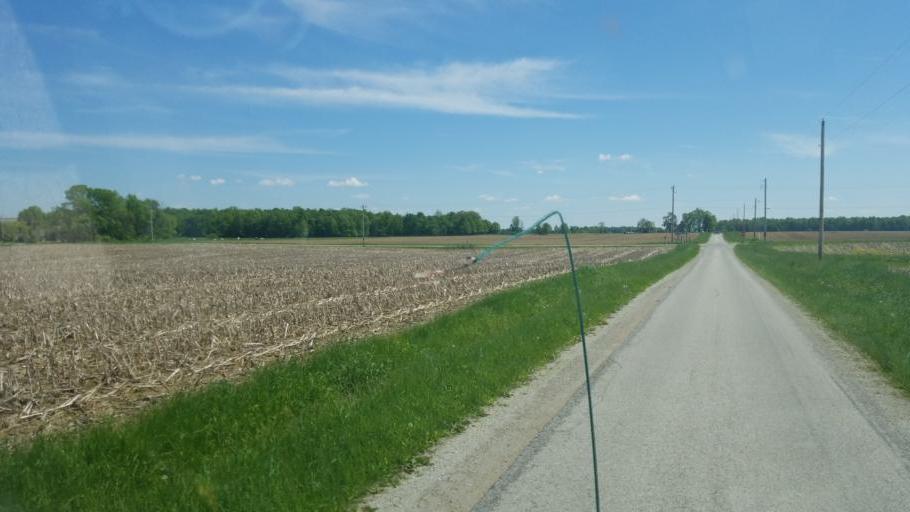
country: US
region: Ohio
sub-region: Huron County
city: Willard
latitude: 41.0581
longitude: -82.9389
